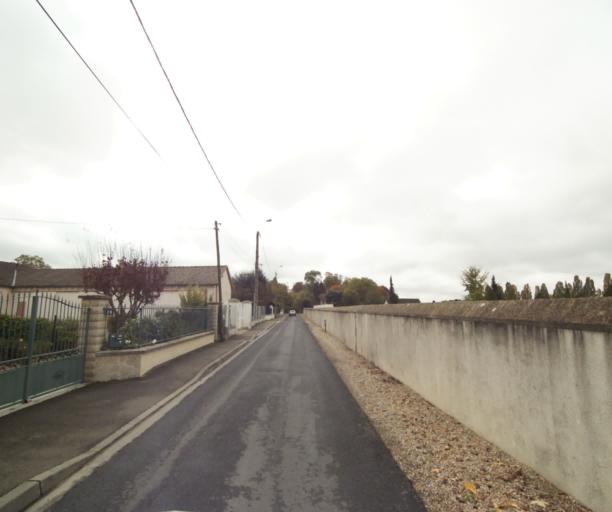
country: FR
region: Centre
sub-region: Departement d'Eure-et-Loir
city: Dreux
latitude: 48.7423
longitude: 1.3674
